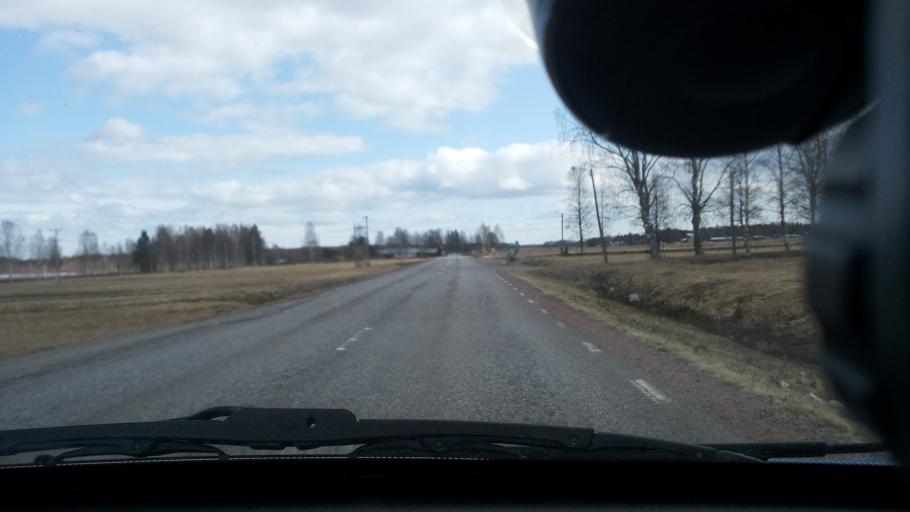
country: SE
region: Norrbotten
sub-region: Lulea Kommun
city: Sodra Sunderbyn
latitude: 65.6581
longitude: 21.8415
